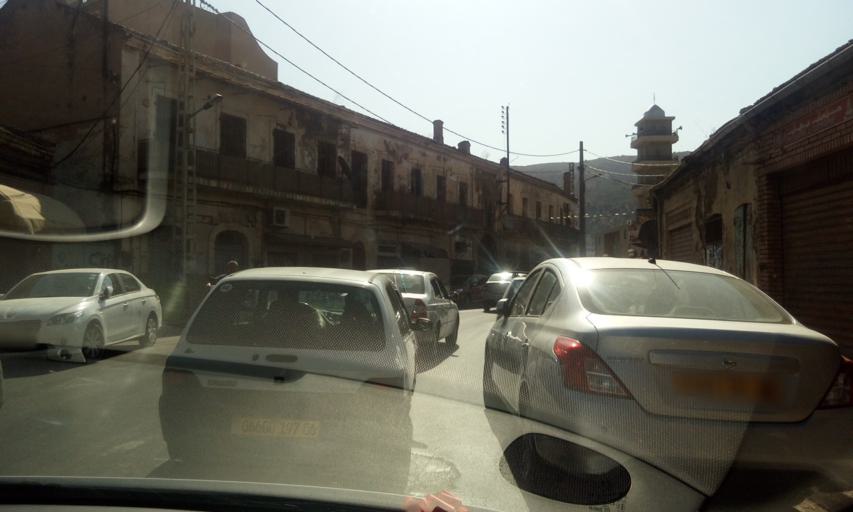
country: DZ
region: Bejaia
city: Seddouk
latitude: 36.6125
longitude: 4.6853
